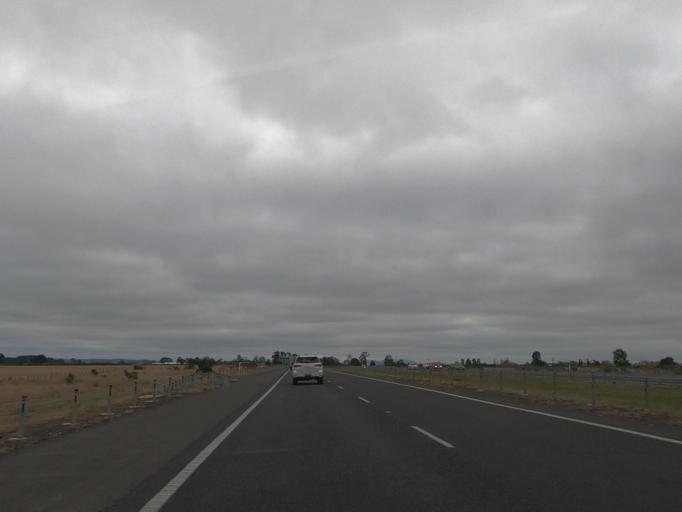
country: AU
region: Victoria
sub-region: Mount Alexander
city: Castlemaine
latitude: -37.2066
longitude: 144.4098
